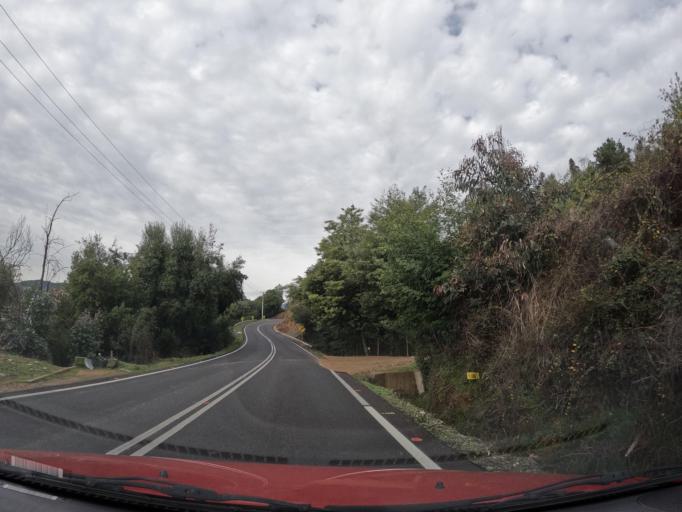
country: CL
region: Maule
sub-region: Provincia de Linares
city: Linares
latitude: -35.9217
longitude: -71.4526
